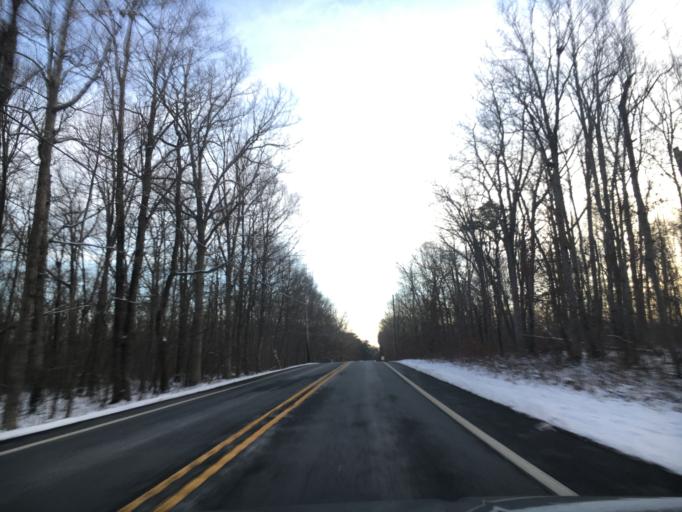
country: US
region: Pennsylvania
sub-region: Pike County
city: Saw Creek
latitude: 41.2009
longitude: -75.0819
